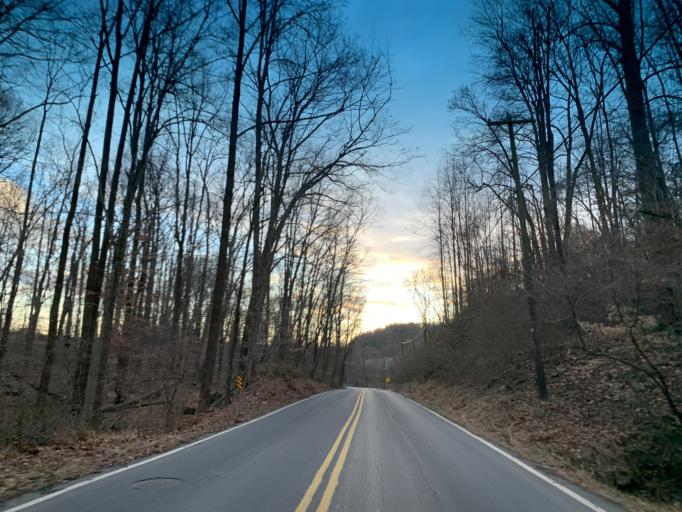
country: US
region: Maryland
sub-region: Harford County
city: Bel Air North
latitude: 39.6391
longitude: -76.3029
